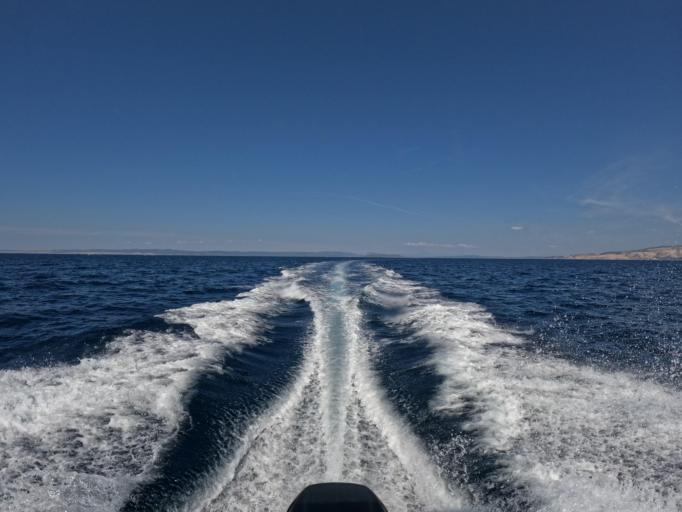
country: HR
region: Primorsko-Goranska
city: Lopar
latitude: 44.8740
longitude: 14.6646
